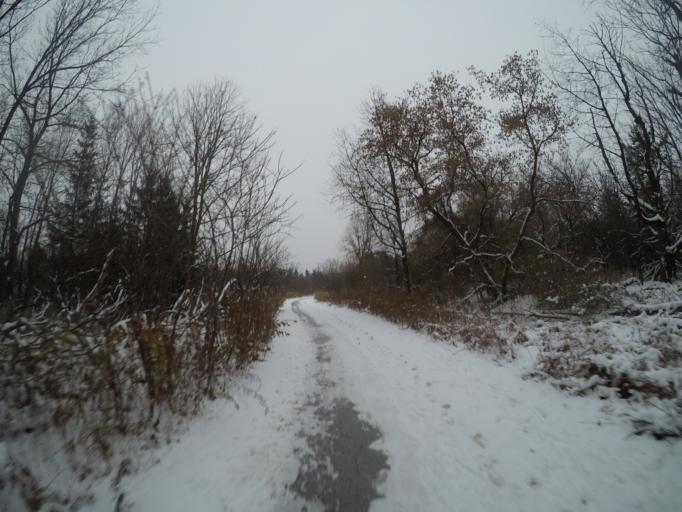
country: CA
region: Ontario
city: Waterloo
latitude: 43.4860
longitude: -80.5061
